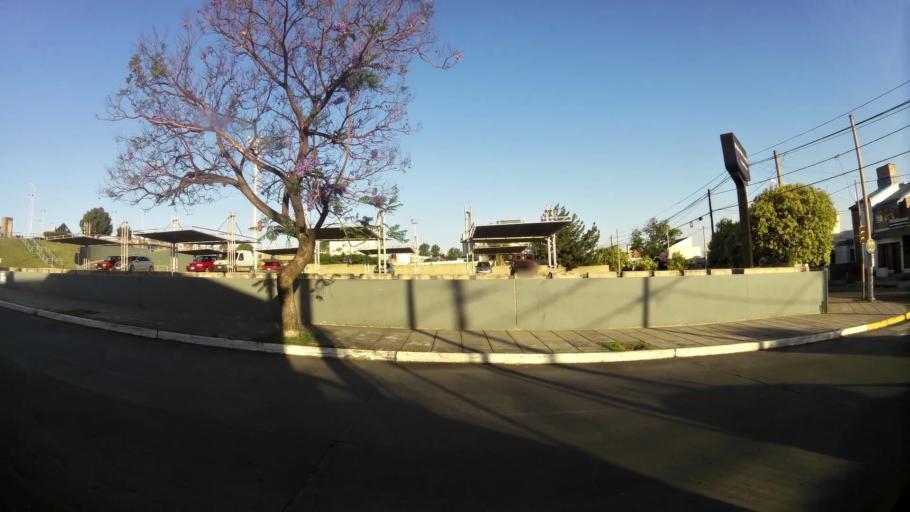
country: AR
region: Cordoba
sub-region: Departamento de Capital
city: Cordoba
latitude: -31.3823
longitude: -64.2161
